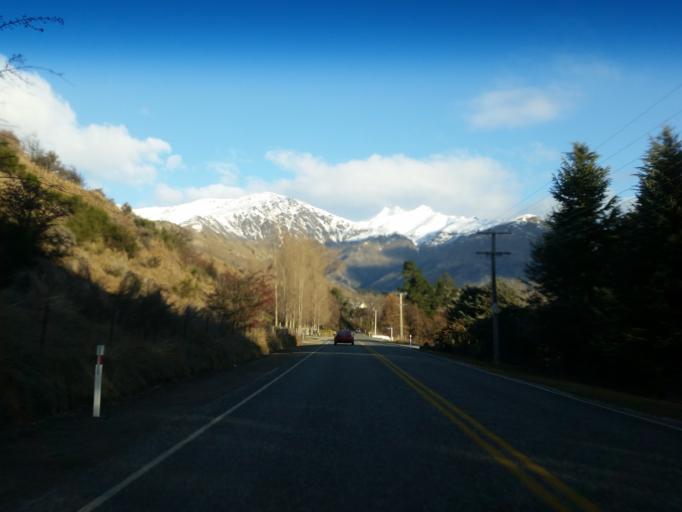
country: NZ
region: Otago
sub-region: Queenstown-Lakes District
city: Arrowtown
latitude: -44.9667
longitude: 168.8178
